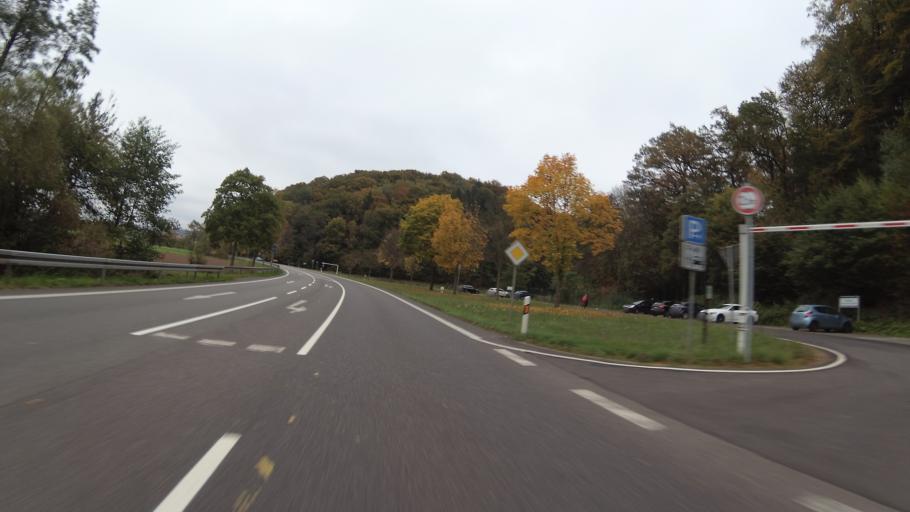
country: DE
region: Saarland
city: Blieskastel
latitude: 49.2589
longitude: 7.3056
